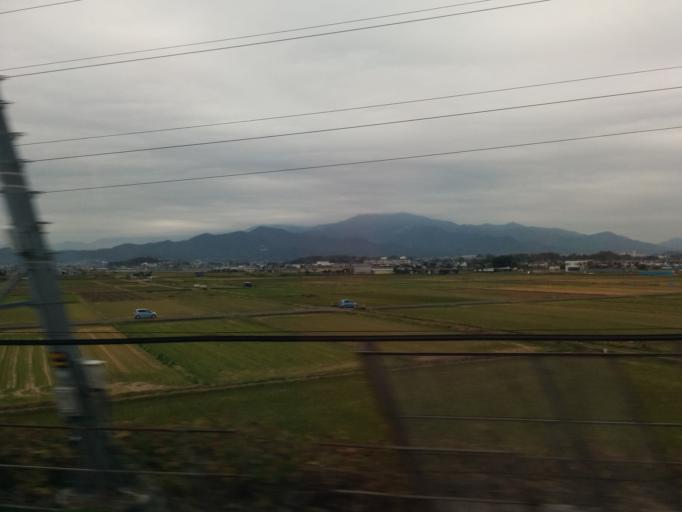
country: JP
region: Kanagawa
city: Isehara
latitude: 35.3646
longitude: 139.3328
